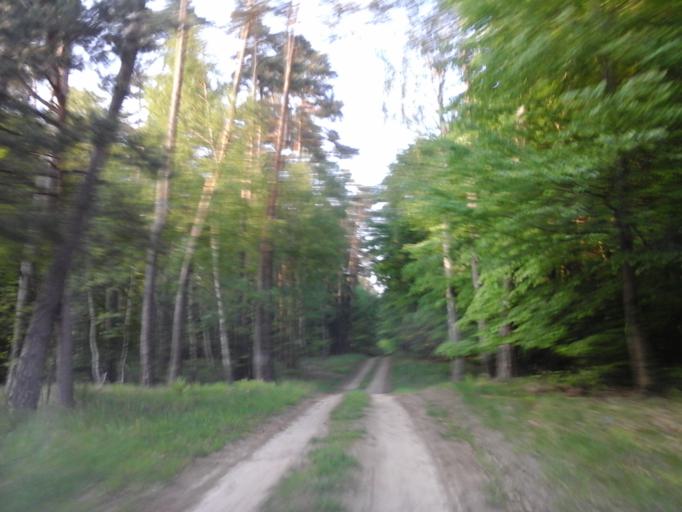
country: PL
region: West Pomeranian Voivodeship
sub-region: Powiat choszczenski
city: Krzecin
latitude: 53.0102
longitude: 15.5409
